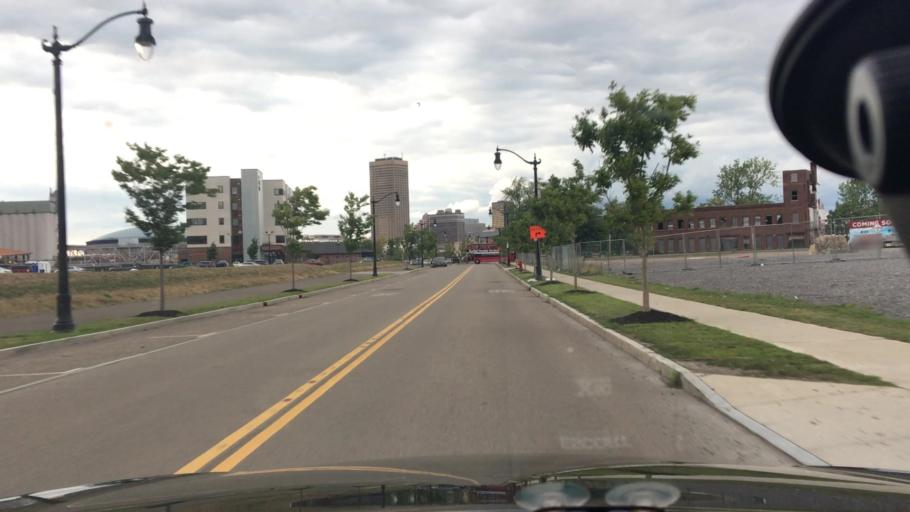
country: US
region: New York
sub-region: Erie County
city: Buffalo
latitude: 42.8679
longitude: -78.8684
